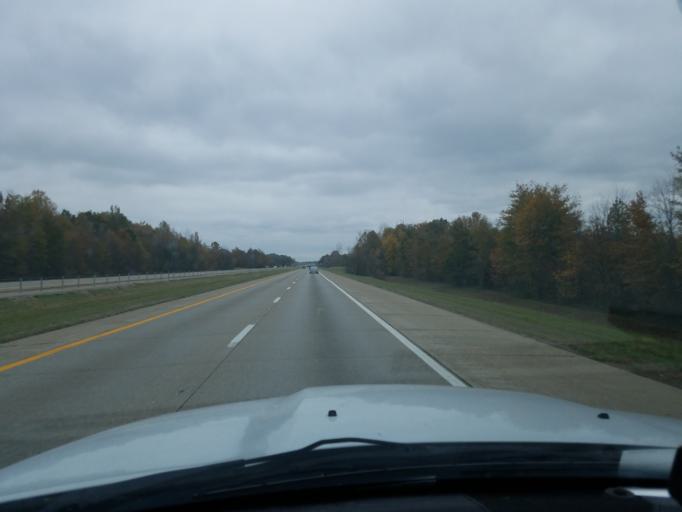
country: US
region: Kentucky
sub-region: Jefferson County
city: Fairdale
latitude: 38.1120
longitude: -85.7998
